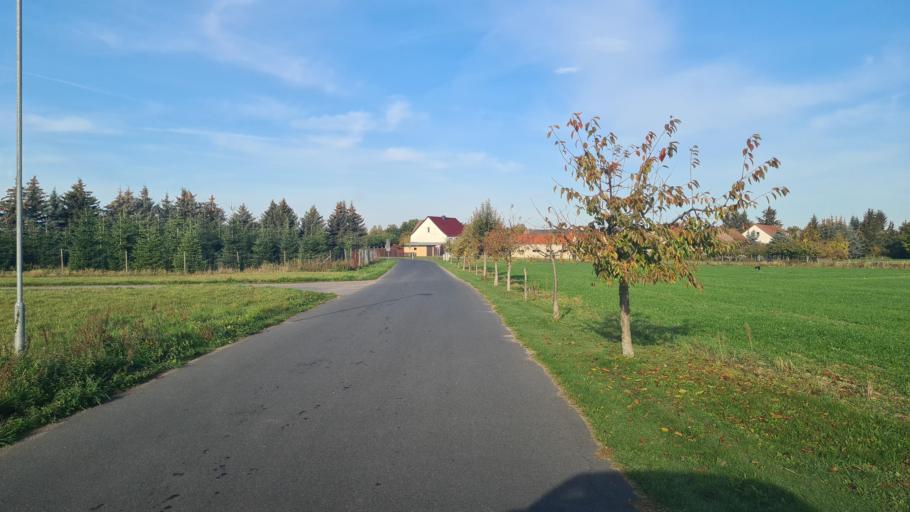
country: DE
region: Brandenburg
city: Dahme
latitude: 51.8814
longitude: 13.3830
